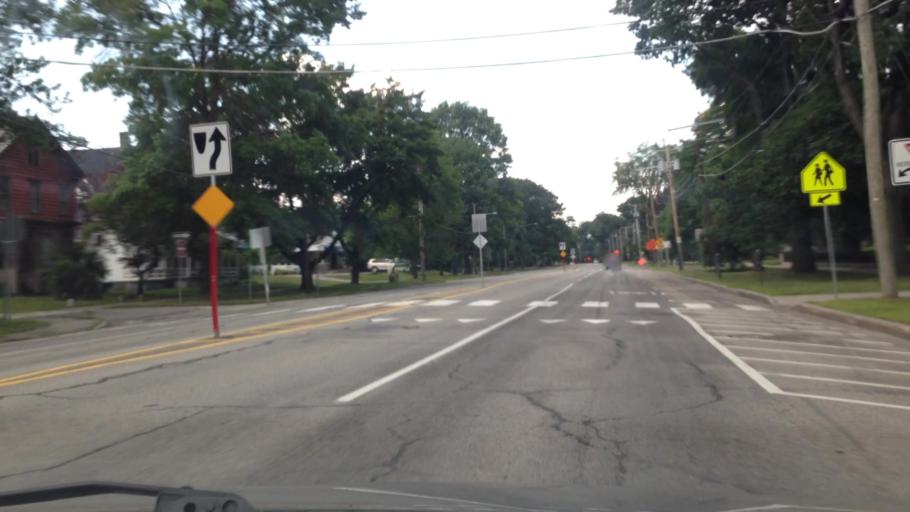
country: US
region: New Hampshire
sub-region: Cheshire County
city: Keene
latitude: 42.9270
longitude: -72.2774
